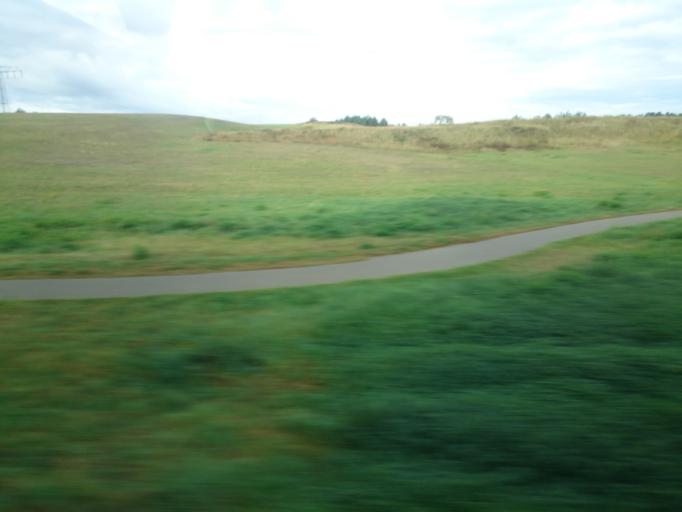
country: DE
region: Mecklenburg-Vorpommern
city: Jatznick
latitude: 53.5563
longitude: 13.9670
